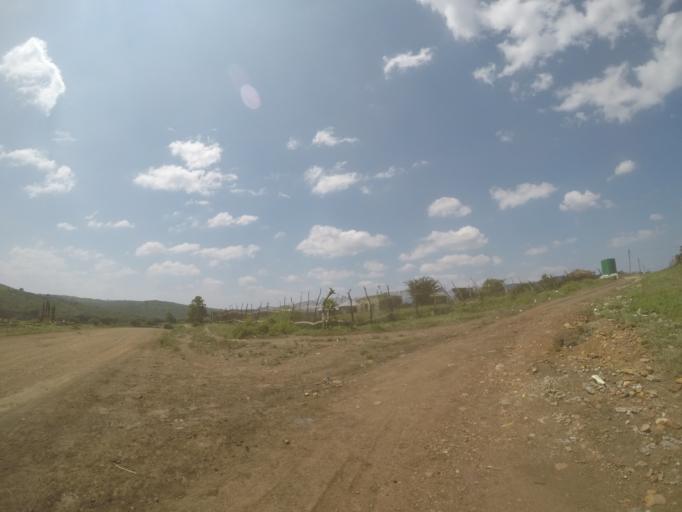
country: ZA
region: KwaZulu-Natal
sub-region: uThungulu District Municipality
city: Empangeni
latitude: -28.5912
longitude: 31.7364
